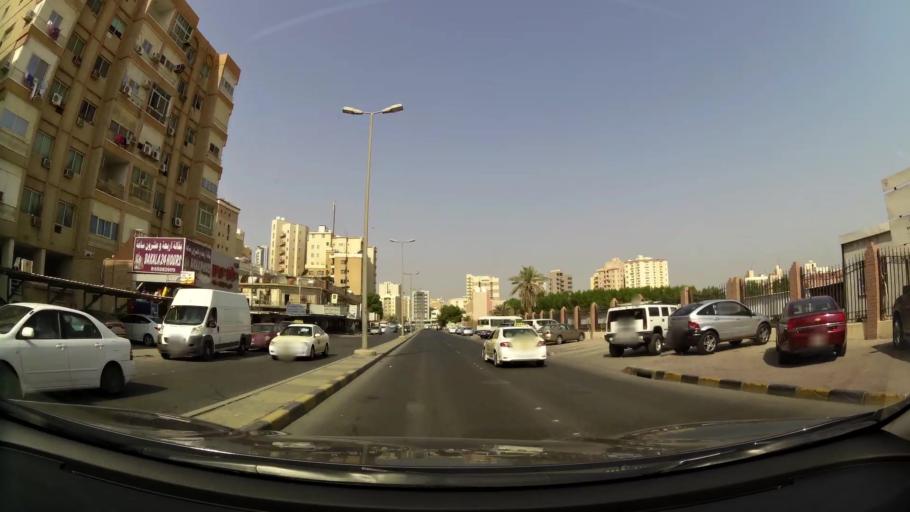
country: KW
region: Muhafazat Hawalli
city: Hawalli
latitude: 29.3435
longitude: 48.0216
